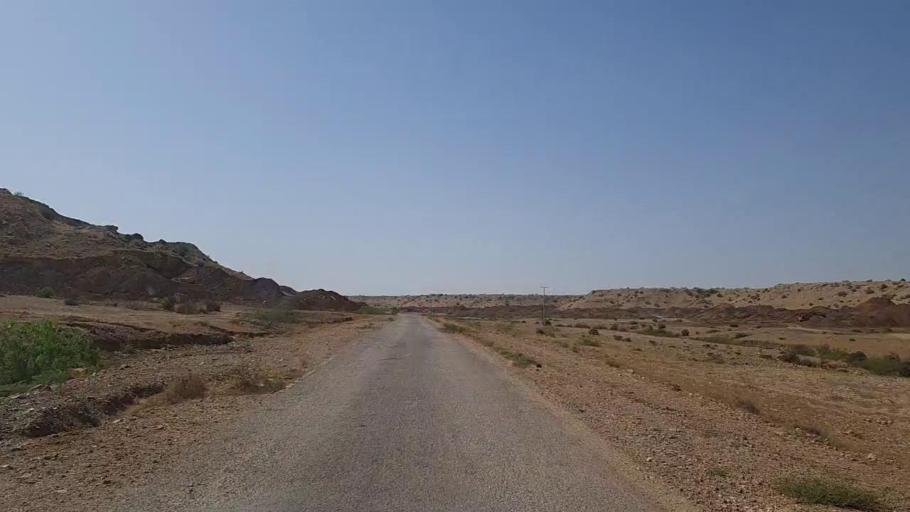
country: PK
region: Sindh
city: Kotri
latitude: 25.1612
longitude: 68.2157
